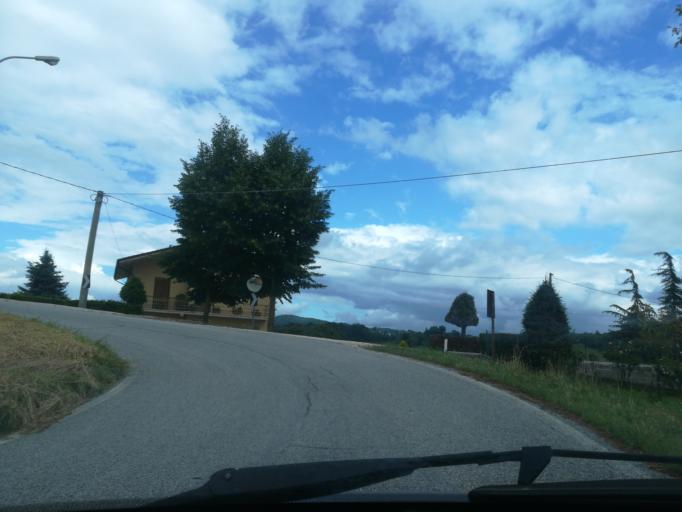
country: IT
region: The Marches
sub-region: Province of Fermo
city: Montefortino
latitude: 42.9355
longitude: 13.3741
